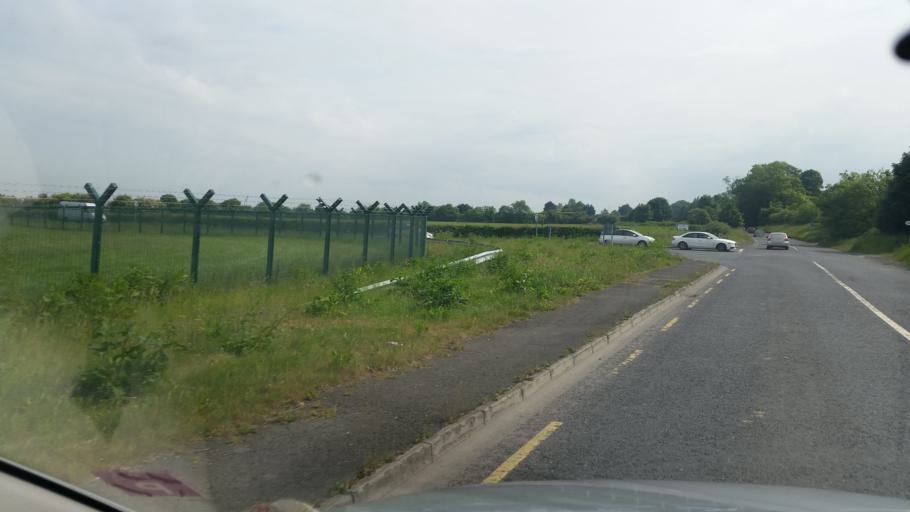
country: IE
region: Leinster
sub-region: Dublin City
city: Finglas
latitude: 53.4225
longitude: -6.3062
